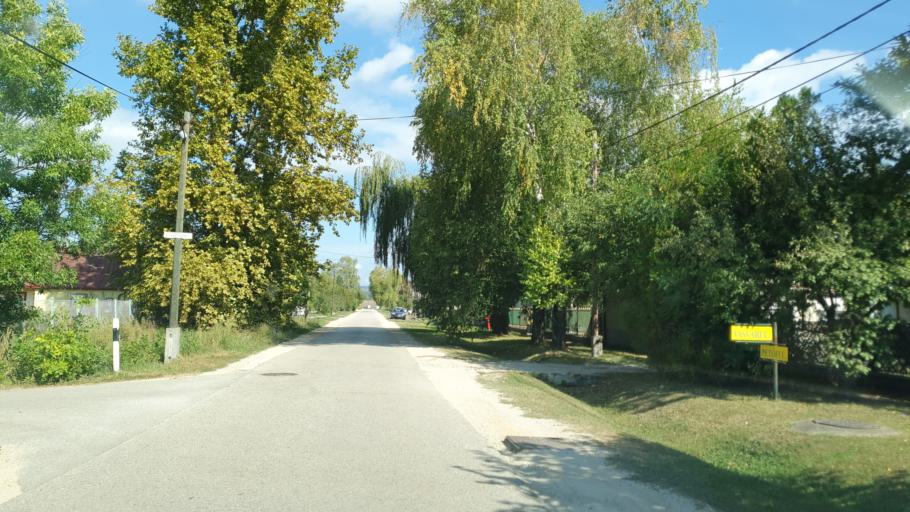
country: HU
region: Fejer
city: Zamoly
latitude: 47.3225
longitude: 18.4077
